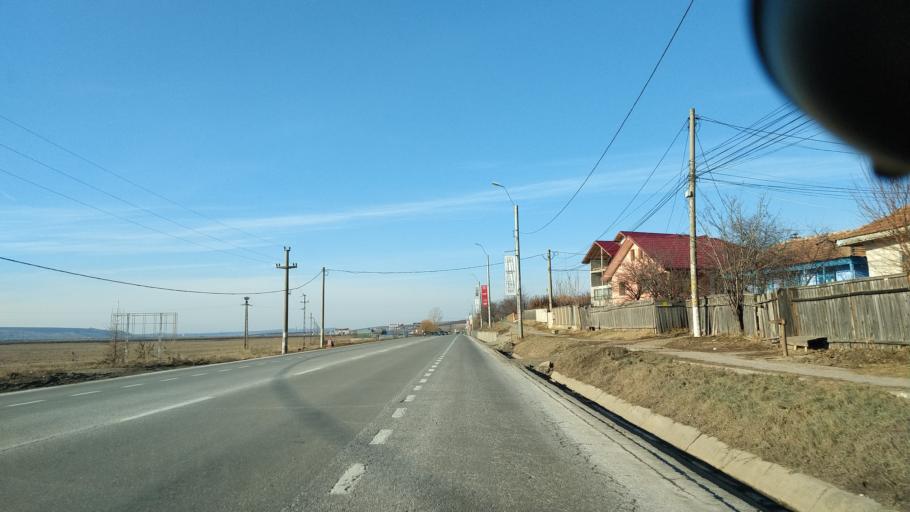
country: RO
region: Iasi
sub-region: Comuna Letcani
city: Letcani
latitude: 47.2003
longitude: 27.3883
